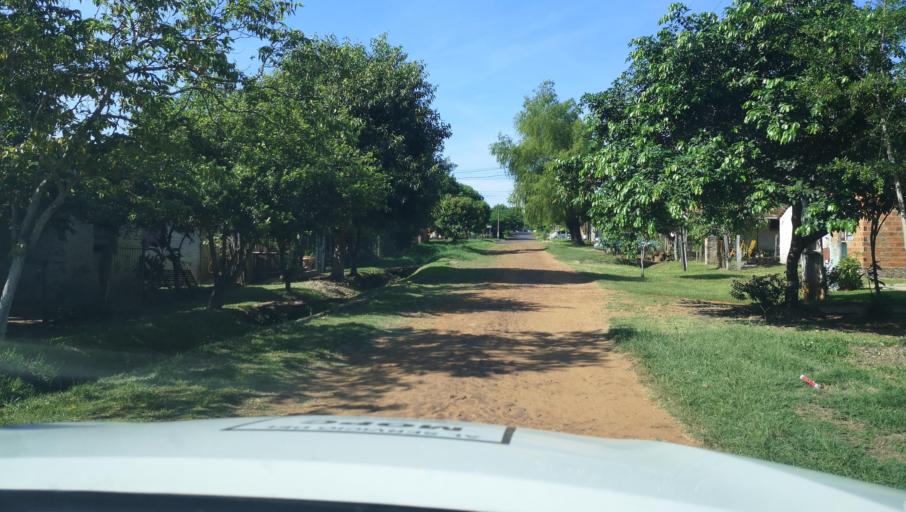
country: PY
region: Misiones
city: Santa Maria
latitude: -26.8843
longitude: -57.0164
